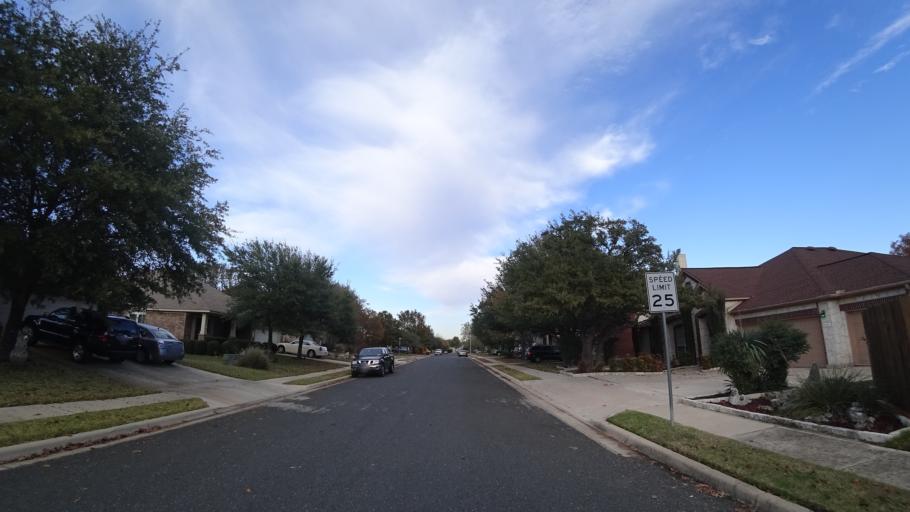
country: US
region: Texas
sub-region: Williamson County
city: Brushy Creek
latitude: 30.4989
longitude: -97.7390
